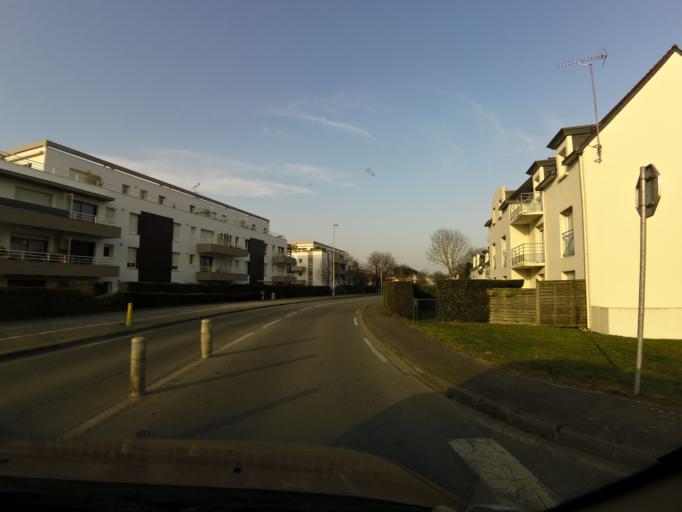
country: FR
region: Brittany
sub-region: Departement du Morbihan
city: Vannes
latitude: 47.6561
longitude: -2.7394
